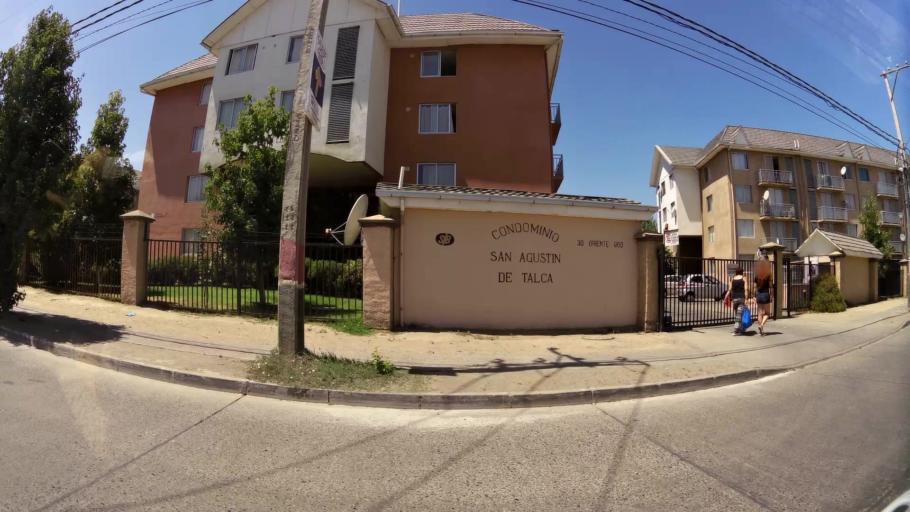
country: CL
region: Maule
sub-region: Provincia de Talca
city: Talca
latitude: -35.4358
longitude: -71.6301
